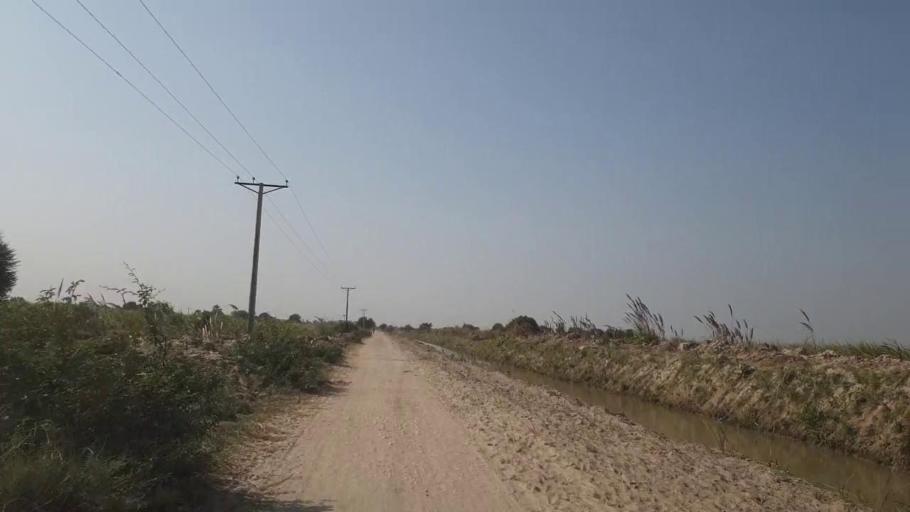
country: PK
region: Sindh
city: Bulri
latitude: 24.9514
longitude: 68.3730
